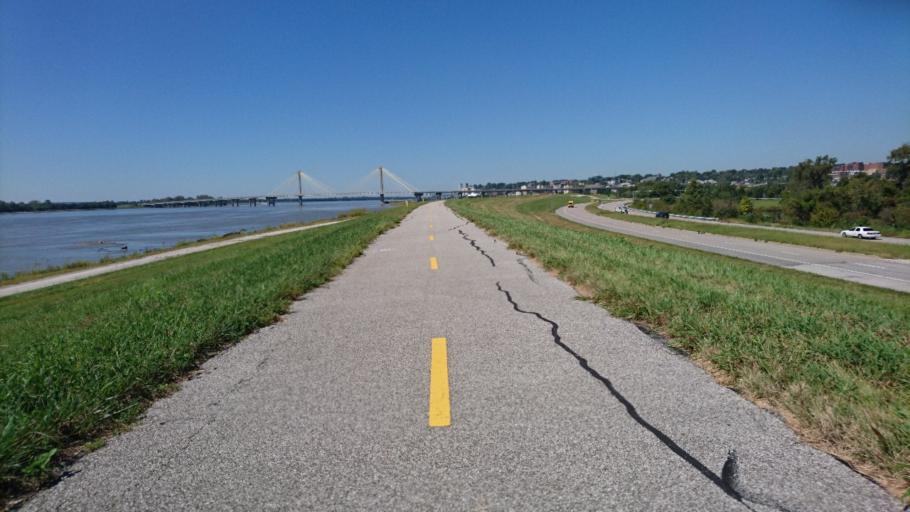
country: US
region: Illinois
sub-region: Madison County
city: Alton
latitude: 38.8797
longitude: -90.1635
